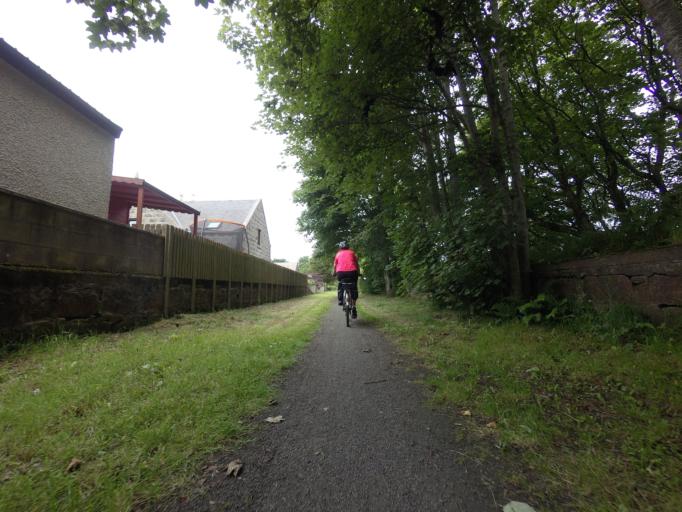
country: GB
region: Scotland
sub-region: Aberdeenshire
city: Ellon
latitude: 57.4665
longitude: -2.1169
